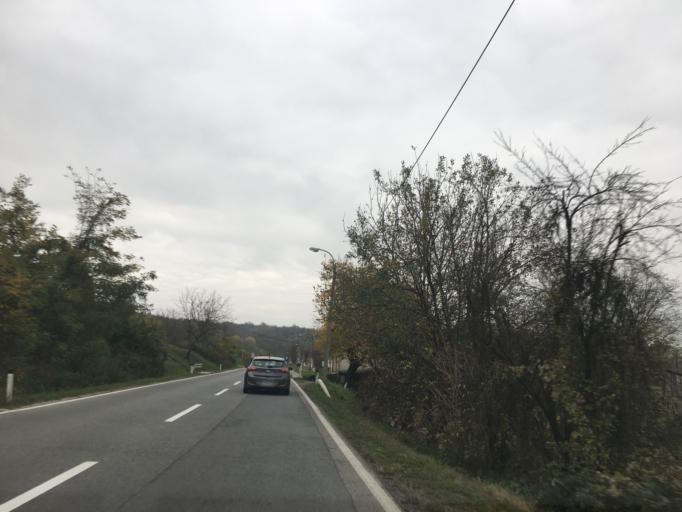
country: RS
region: Central Serbia
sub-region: Raski Okrug
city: Kraljevo
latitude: 43.7201
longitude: 20.7756
